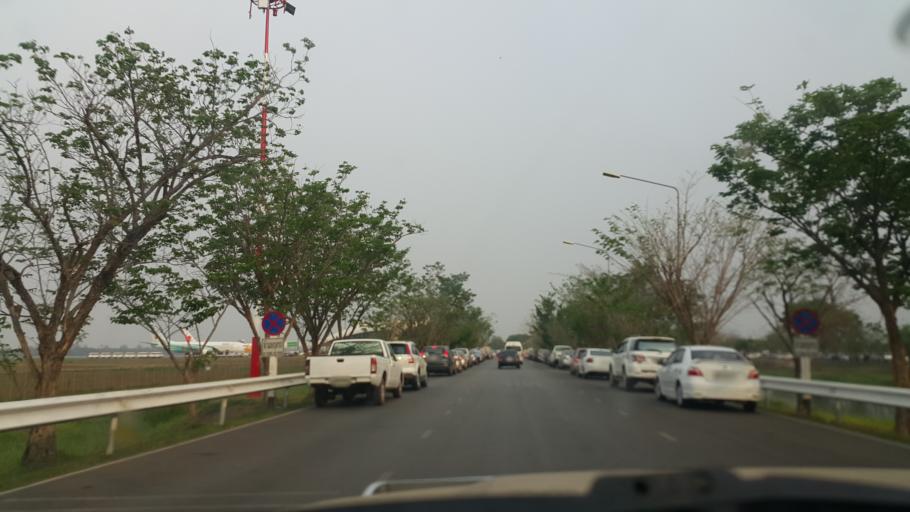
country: TH
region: Changwat Udon Thani
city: Udon Thani
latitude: 17.3880
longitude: 102.7724
